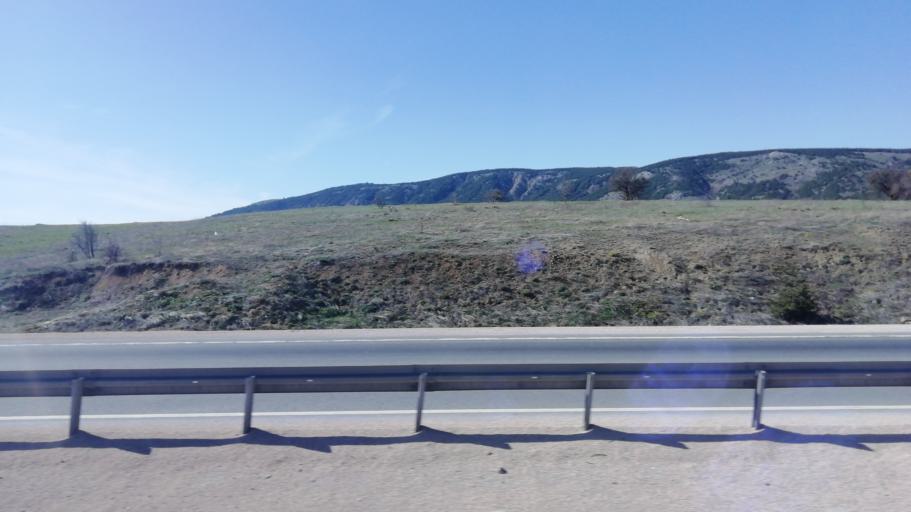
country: TR
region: Karabuk
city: Gozyeri
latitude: 40.8637
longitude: 32.5626
